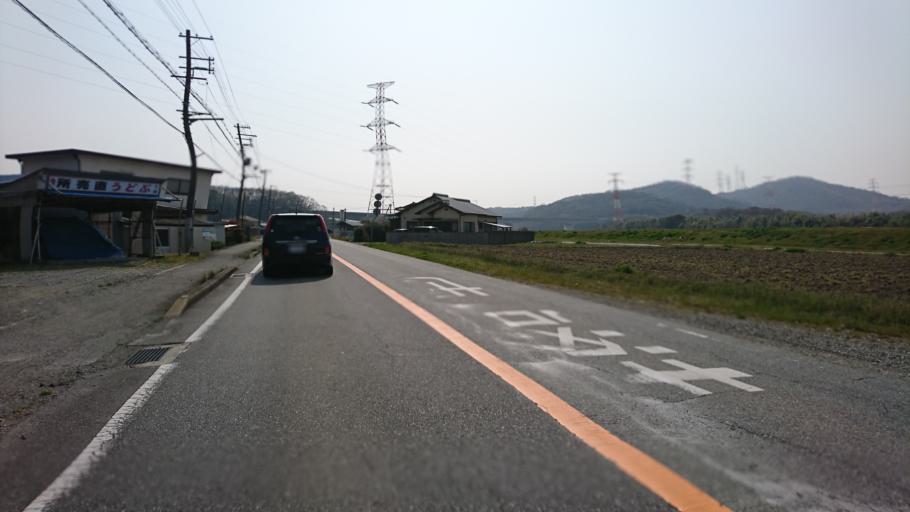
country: JP
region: Hyogo
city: Ono
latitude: 34.8141
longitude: 134.9365
